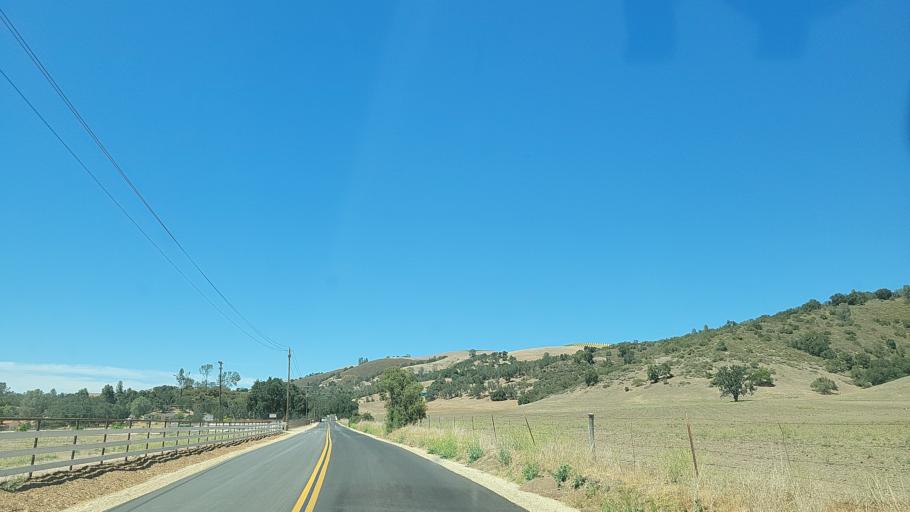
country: US
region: California
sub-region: San Luis Obispo County
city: Atascadero
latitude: 35.4693
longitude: -120.6235
